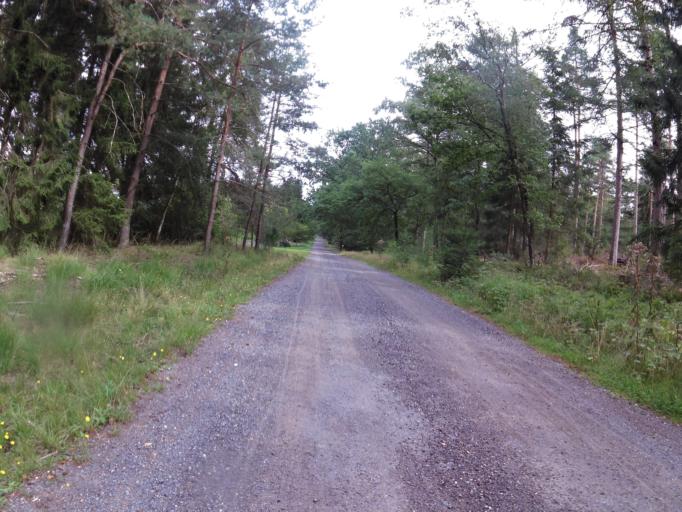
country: DE
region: Lower Saxony
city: Hipstedt
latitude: 53.5009
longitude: 8.9558
